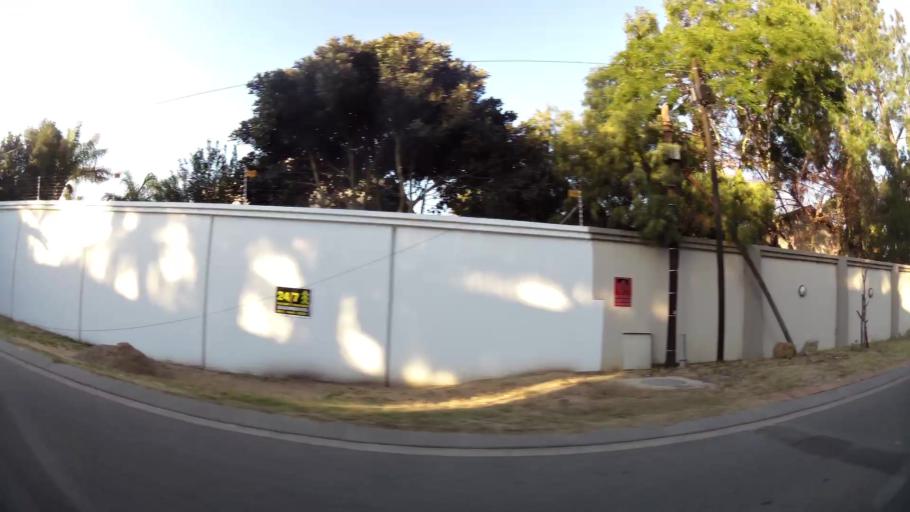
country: ZA
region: Gauteng
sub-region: City of Johannesburg Metropolitan Municipality
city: Modderfontein
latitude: -26.0714
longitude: 28.0613
